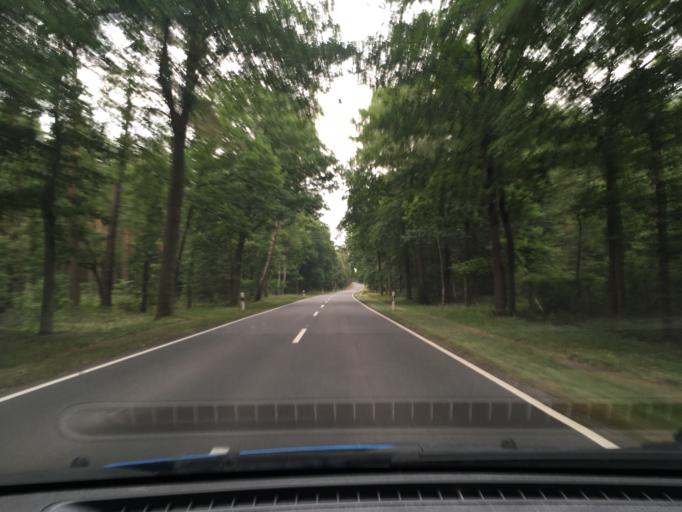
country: DE
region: Lower Saxony
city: Walsrode
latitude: 52.8188
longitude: 9.6043
